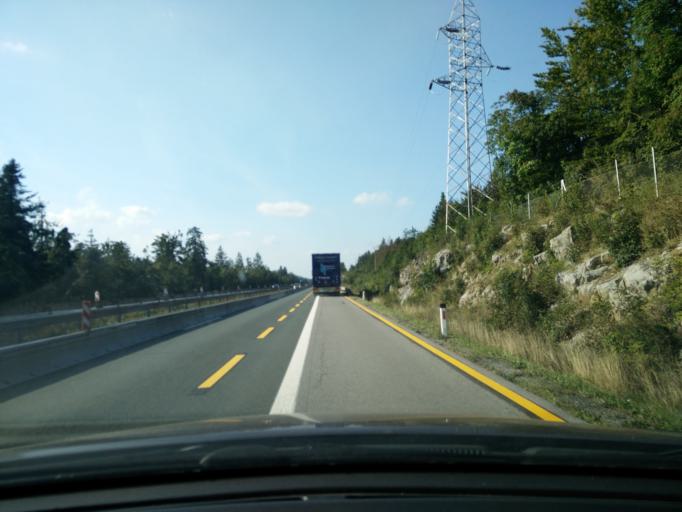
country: SI
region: Cerknica
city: Rakek
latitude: 45.8545
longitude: 14.2807
